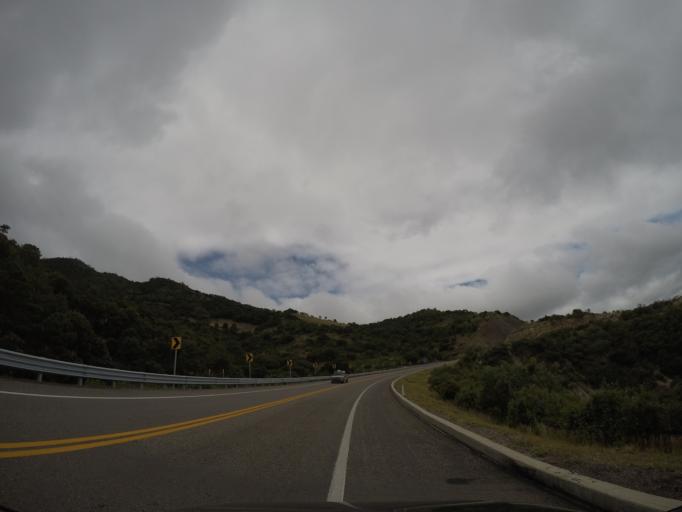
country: MX
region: Oaxaca
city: San Lorenzo Albarradas
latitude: 16.9307
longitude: -96.2667
